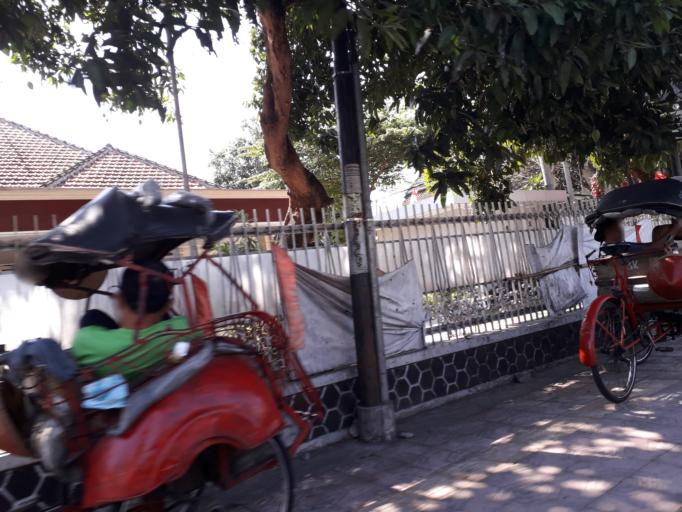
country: ID
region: Daerah Istimewa Yogyakarta
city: Yogyakarta
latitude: -7.7799
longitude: 110.3755
